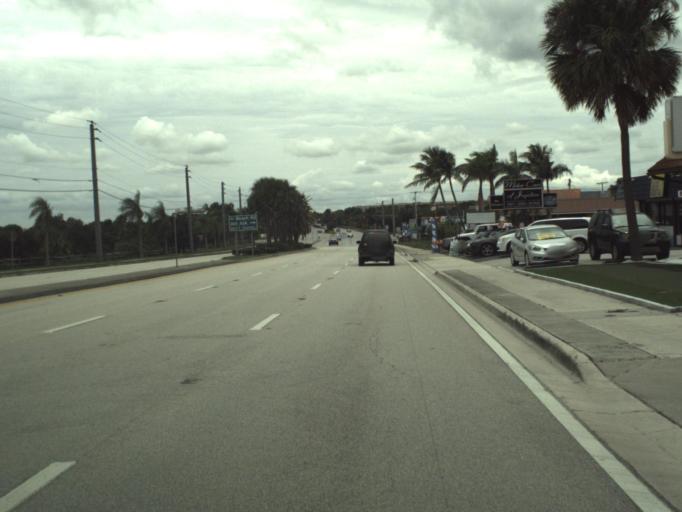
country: US
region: Florida
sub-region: Palm Beach County
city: Jupiter
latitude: 26.9550
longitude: -80.0852
